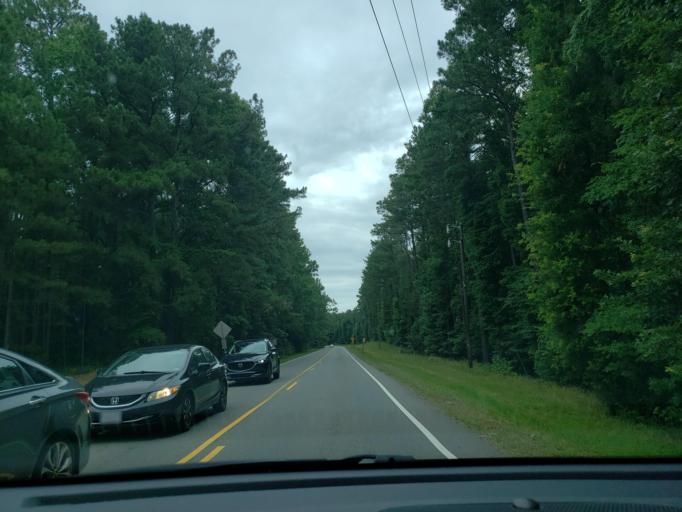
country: US
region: North Carolina
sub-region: Wake County
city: Green Level
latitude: 35.7376
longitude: -79.0004
